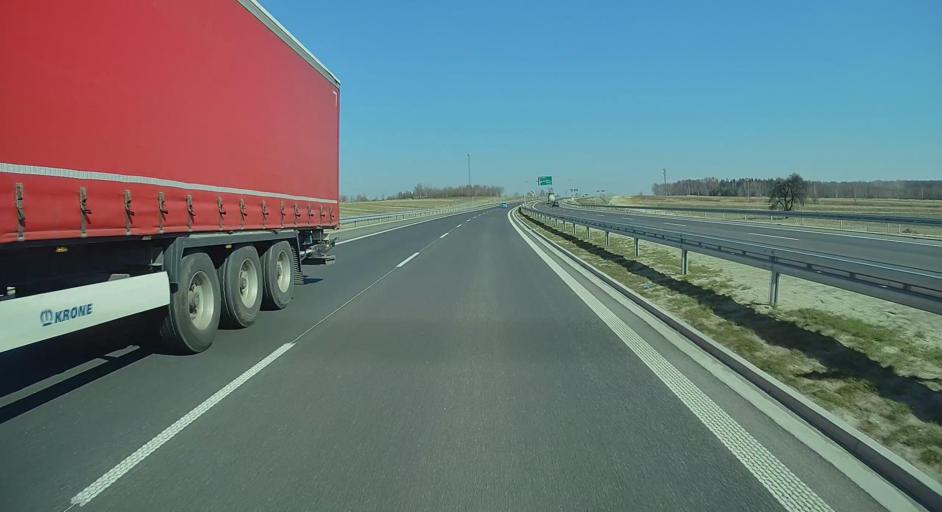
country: PL
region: Subcarpathian Voivodeship
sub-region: Powiat rzeszowski
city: Gorno
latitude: 50.2961
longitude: 22.1183
